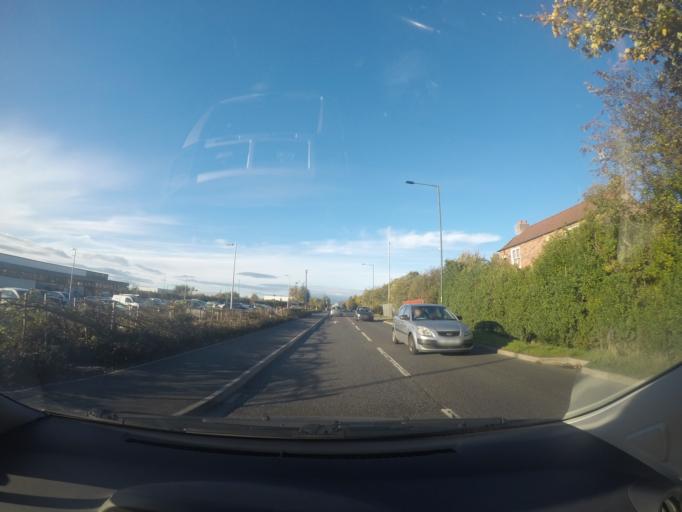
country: GB
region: England
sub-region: City of York
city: York
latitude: 53.9838
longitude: -1.0946
